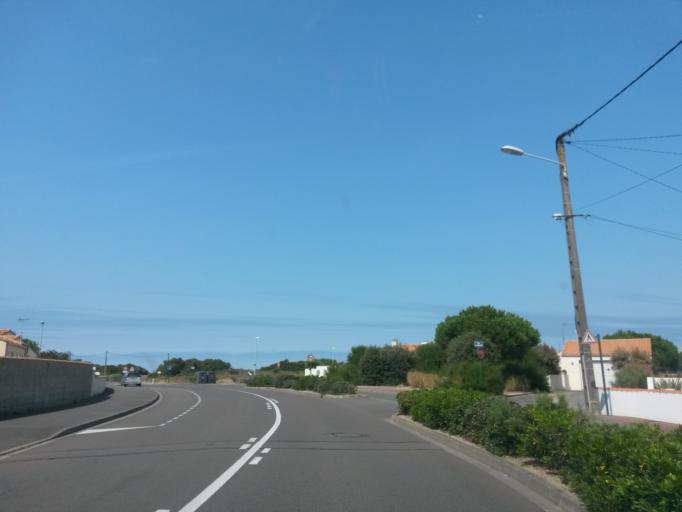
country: FR
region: Pays de la Loire
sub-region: Departement de la Vendee
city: Les Sables-d'Olonne
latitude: 46.5021
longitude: -1.8063
